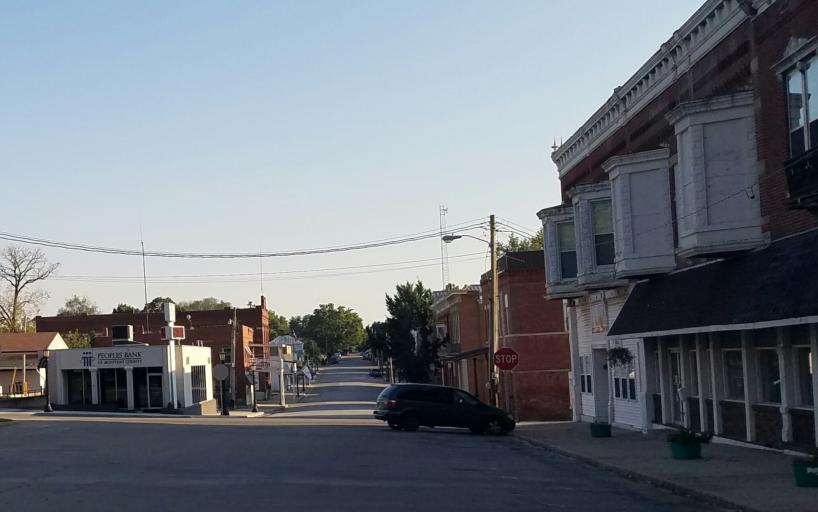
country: US
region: Missouri
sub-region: Moniteau County
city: California
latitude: 38.6367
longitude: -92.5650
